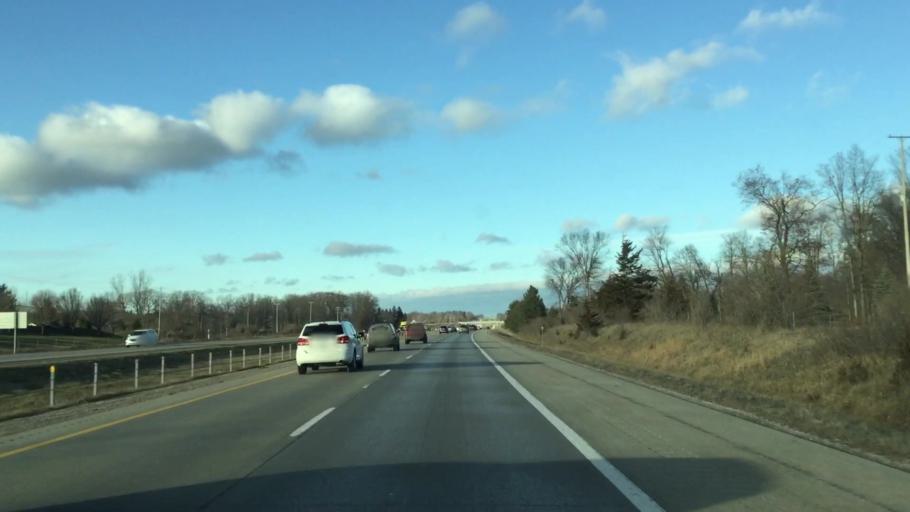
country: US
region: Michigan
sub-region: Genesee County
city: Fenton
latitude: 42.6960
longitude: -83.7611
